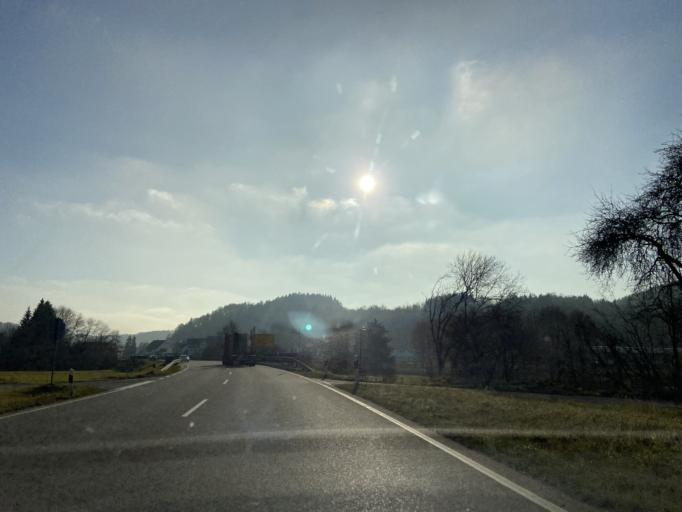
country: DE
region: Baden-Wuerttemberg
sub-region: Tuebingen Region
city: Veringenstadt
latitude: 48.1625
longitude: 9.2002
